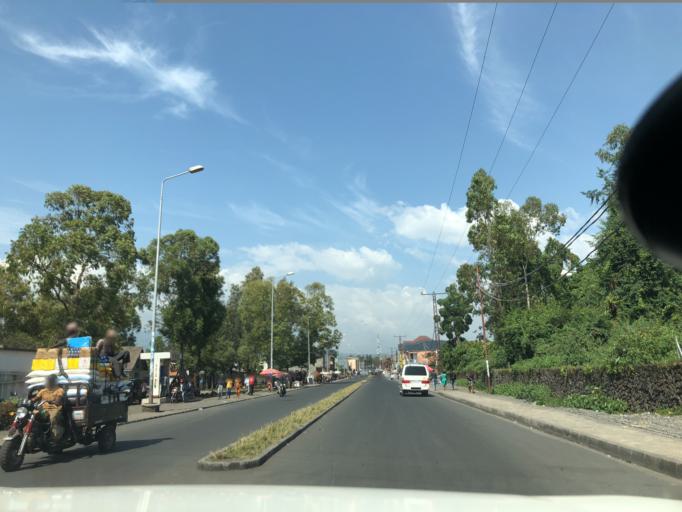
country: CD
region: Nord Kivu
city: Goma
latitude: -1.6631
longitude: 29.1842
